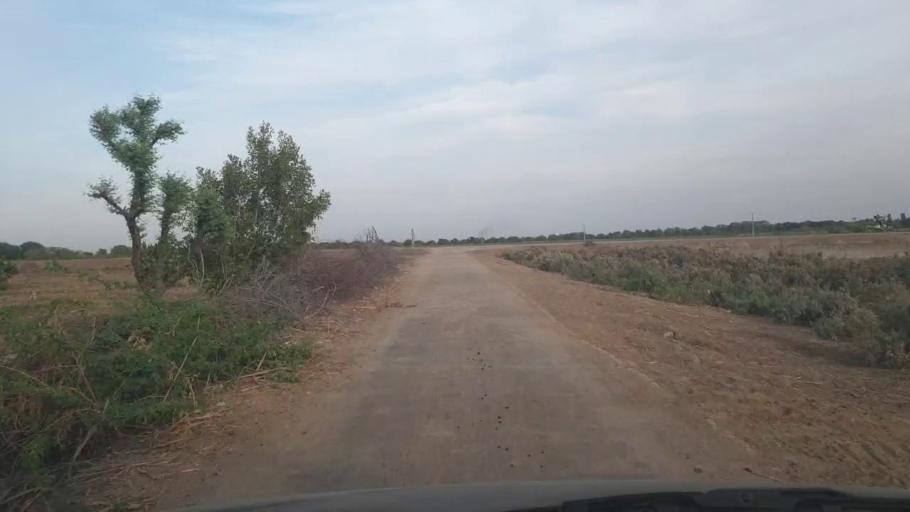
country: PK
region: Sindh
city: Kunri
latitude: 25.2560
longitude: 69.5433
